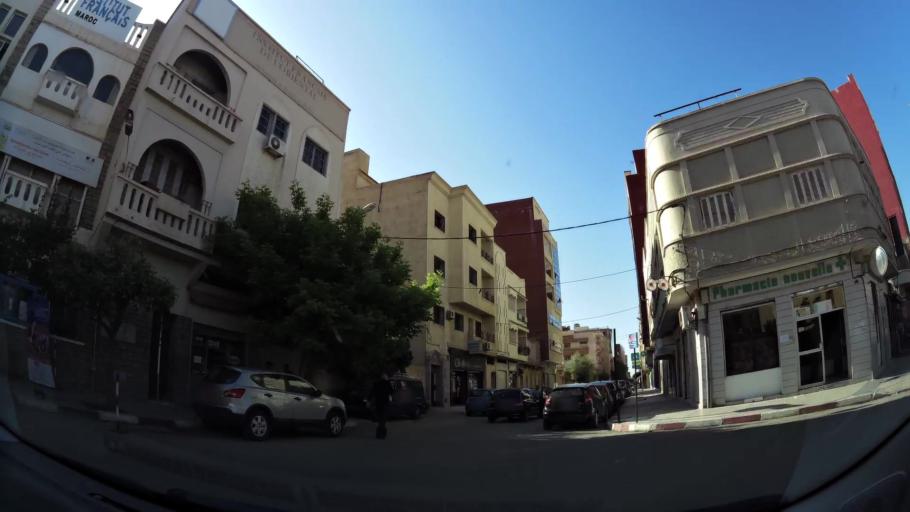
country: MA
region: Oriental
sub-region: Oujda-Angad
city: Oujda
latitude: 34.6850
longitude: -1.9173
